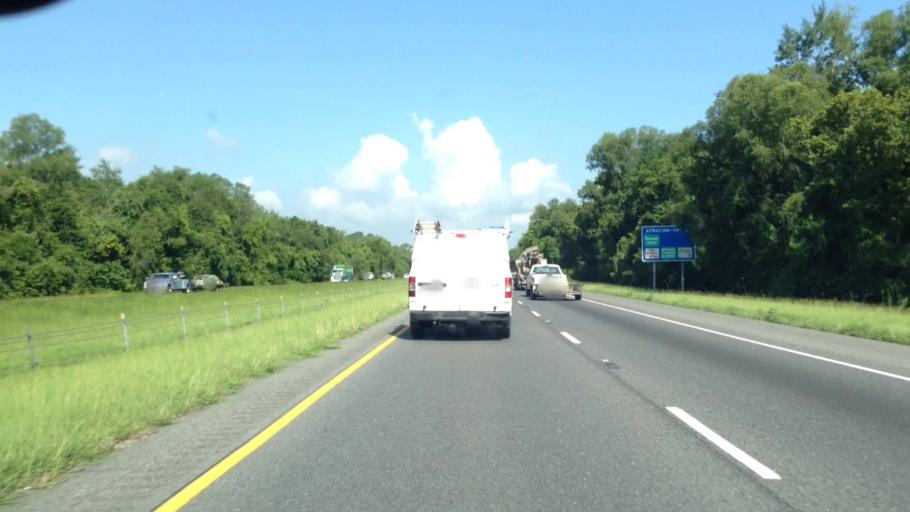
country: US
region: Louisiana
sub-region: Ascension Parish
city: Sorrento
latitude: 30.1647
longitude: -90.8518
